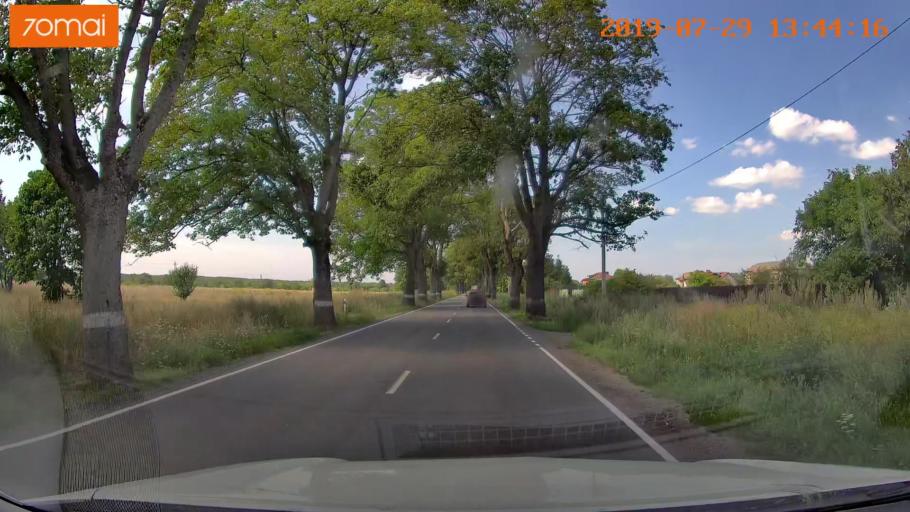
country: RU
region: Kaliningrad
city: Svetlyy
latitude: 54.7375
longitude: 20.0907
